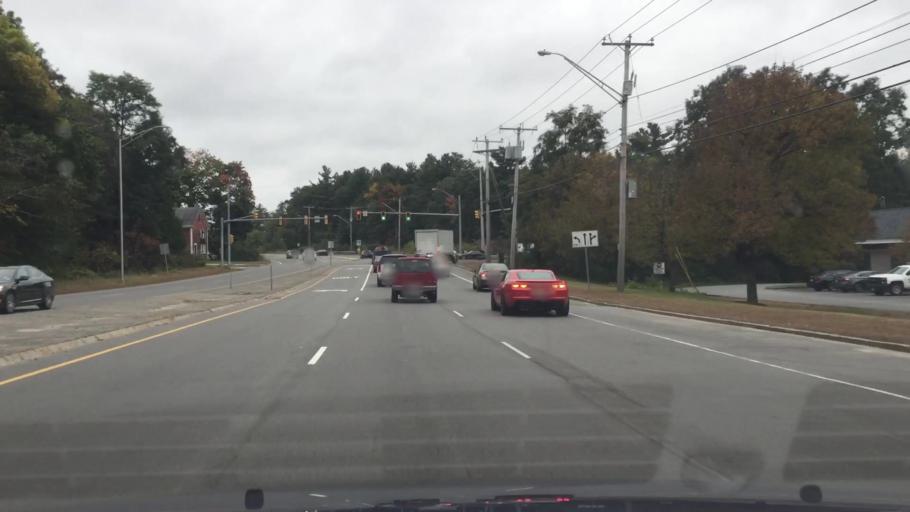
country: US
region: New Hampshire
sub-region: Hillsborough County
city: Hudson
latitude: 42.7244
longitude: -71.4232
